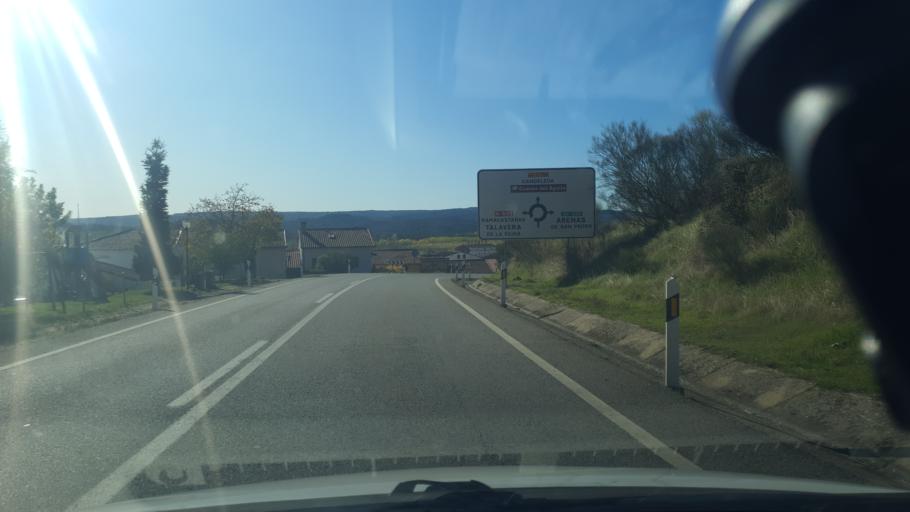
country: ES
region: Castille and Leon
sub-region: Provincia de Avila
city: Arenas de San Pedro
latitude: 40.1874
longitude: -5.0468
